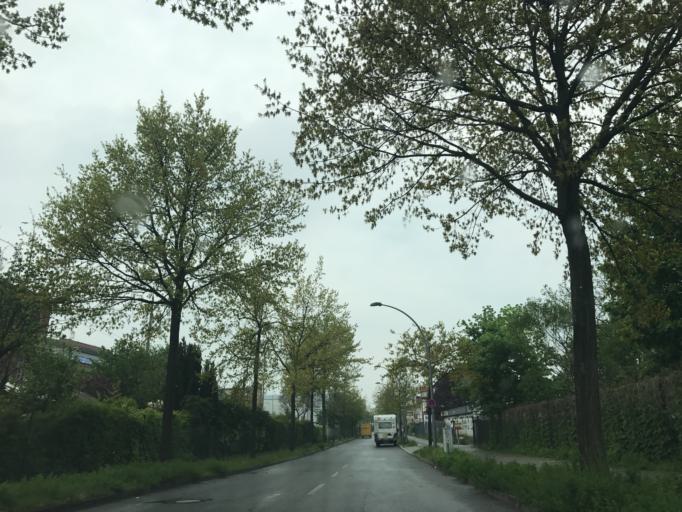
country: DE
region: Berlin
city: Wilhelmstadt
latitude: 52.5357
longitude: 13.1796
